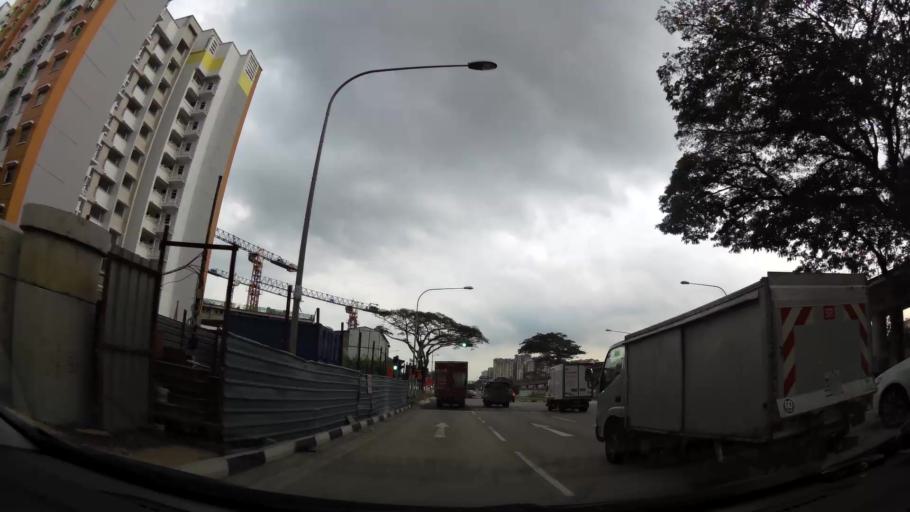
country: MY
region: Johor
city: Kampung Pasir Gudang Baru
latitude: 1.4456
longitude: 103.8286
